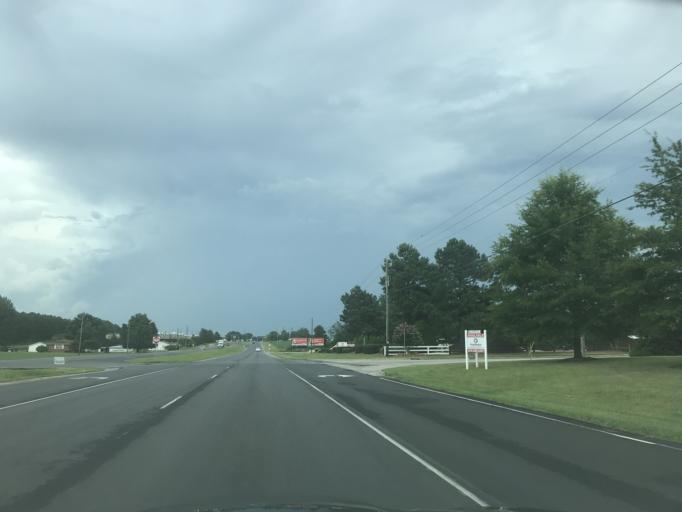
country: US
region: North Carolina
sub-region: Johnston County
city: Clayton
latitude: 35.6305
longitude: -78.4333
